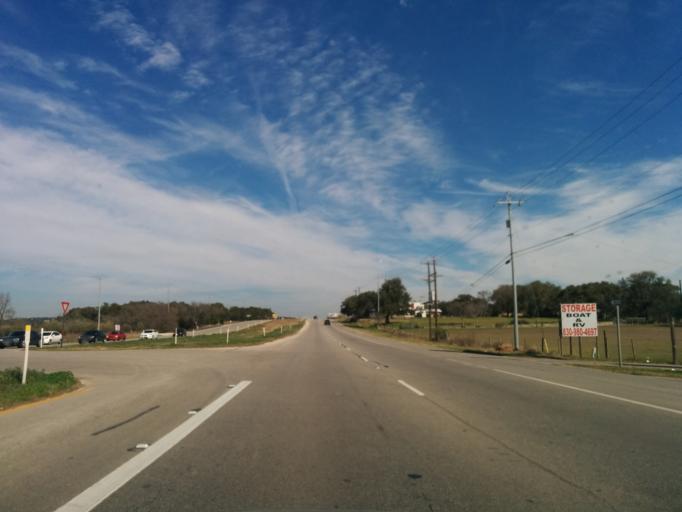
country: US
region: Texas
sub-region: Comal County
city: Bulverde
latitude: 29.7265
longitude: -98.4412
